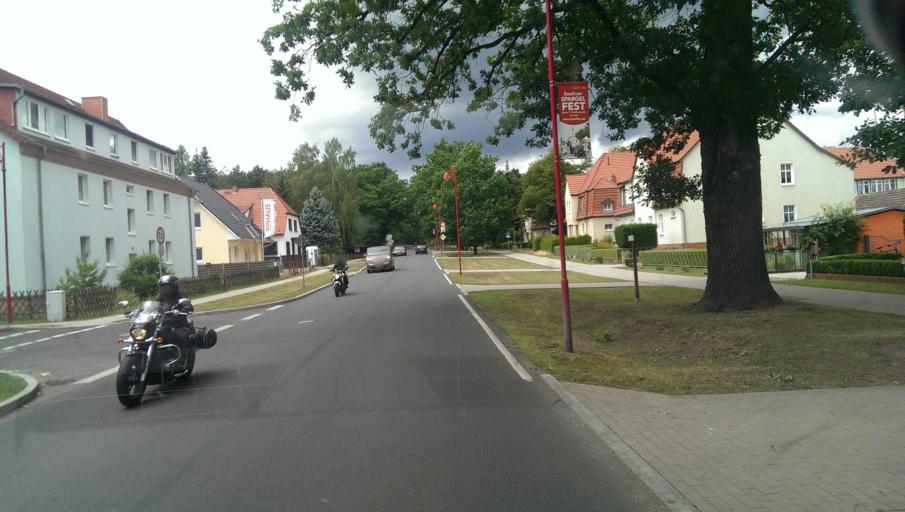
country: DE
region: Brandenburg
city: Beelitz
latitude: 52.2405
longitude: 12.9585
